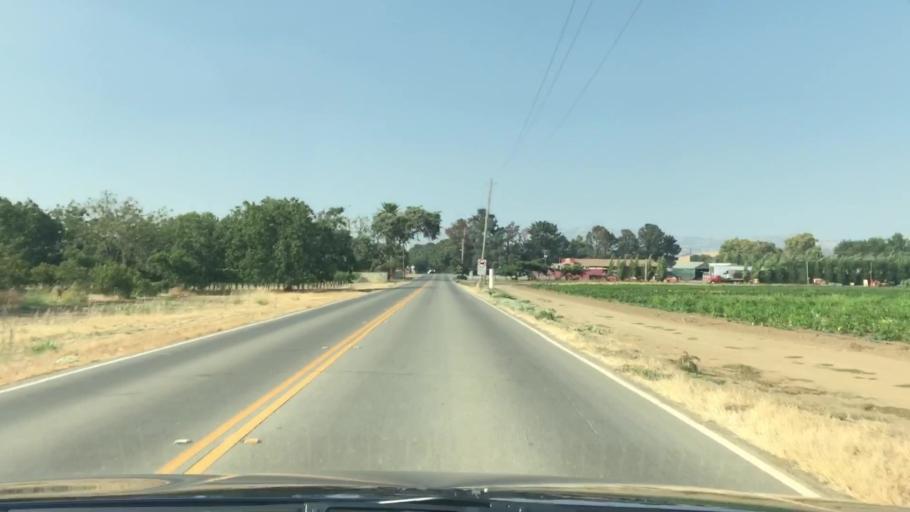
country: US
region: California
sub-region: Solano County
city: Green Valley
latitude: 38.2692
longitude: -122.1124
